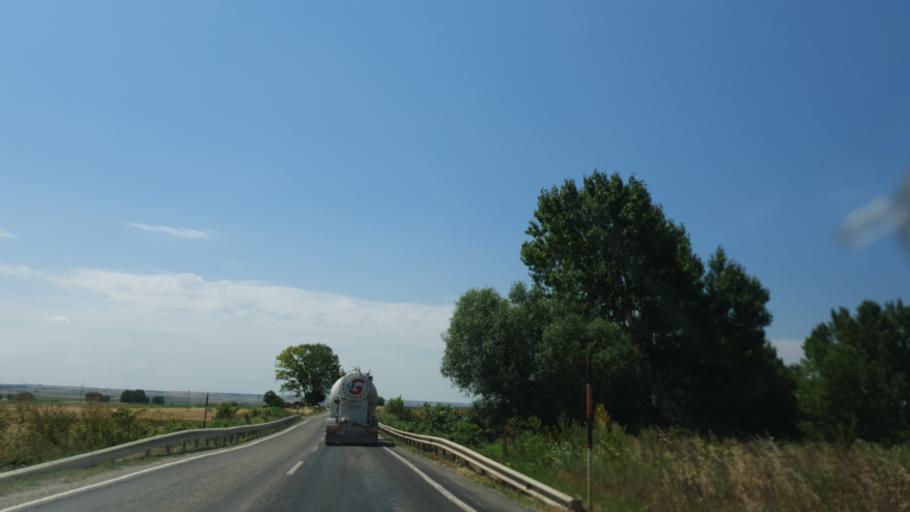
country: TR
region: Kirklareli
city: Vize
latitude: 41.5215
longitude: 27.8514
